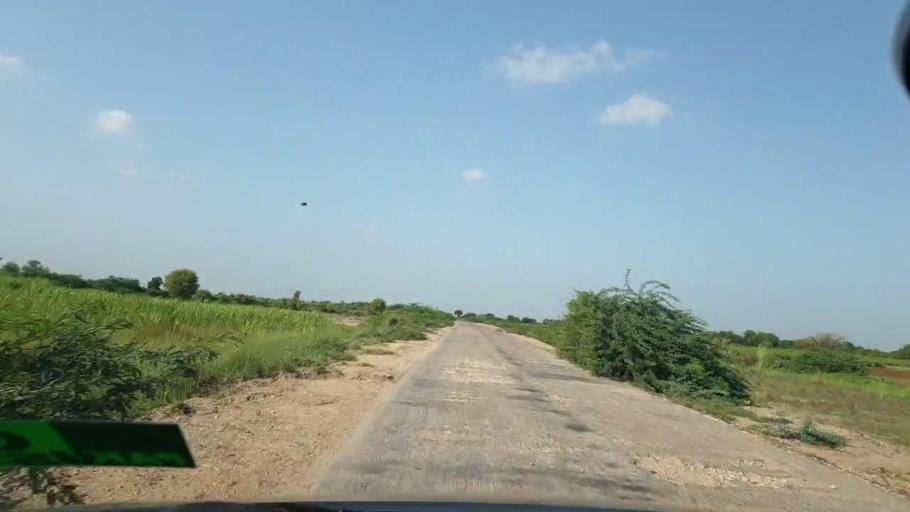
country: PK
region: Sindh
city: Tando Bago
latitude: 24.7150
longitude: 69.1934
